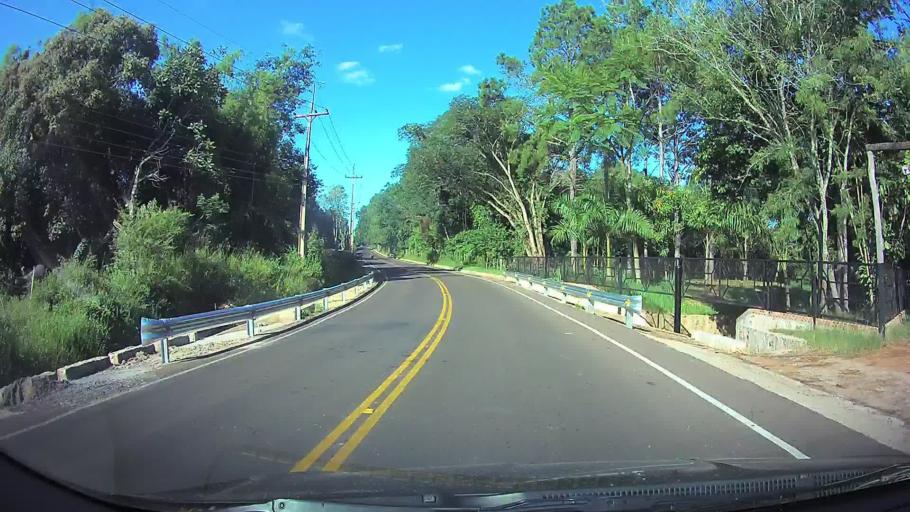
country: PY
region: Cordillera
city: Caacupe
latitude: -25.3214
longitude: -57.1487
